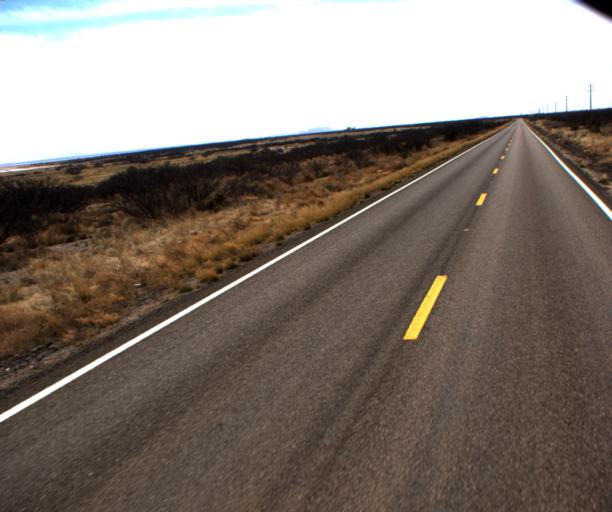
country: US
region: Arizona
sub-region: Cochise County
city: Willcox
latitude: 32.1545
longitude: -109.9383
